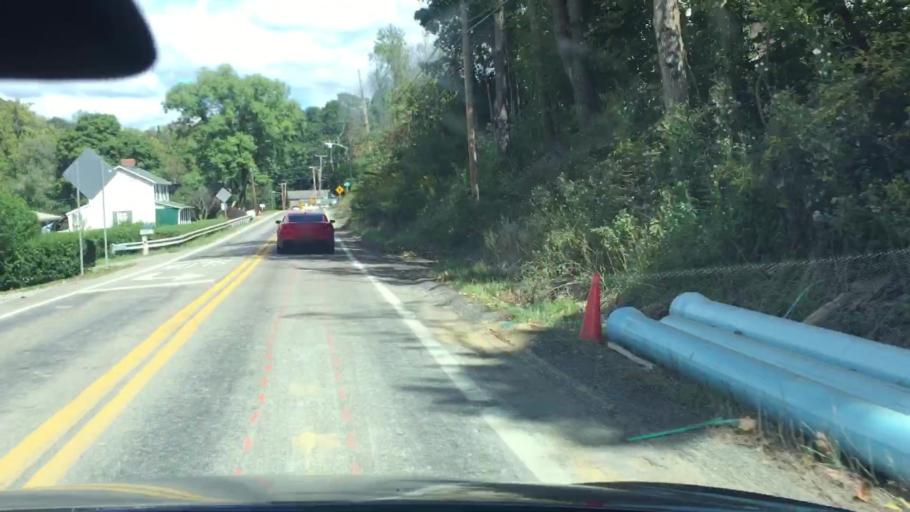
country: US
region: Pennsylvania
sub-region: Allegheny County
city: Russellton
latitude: 40.5878
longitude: -79.8285
